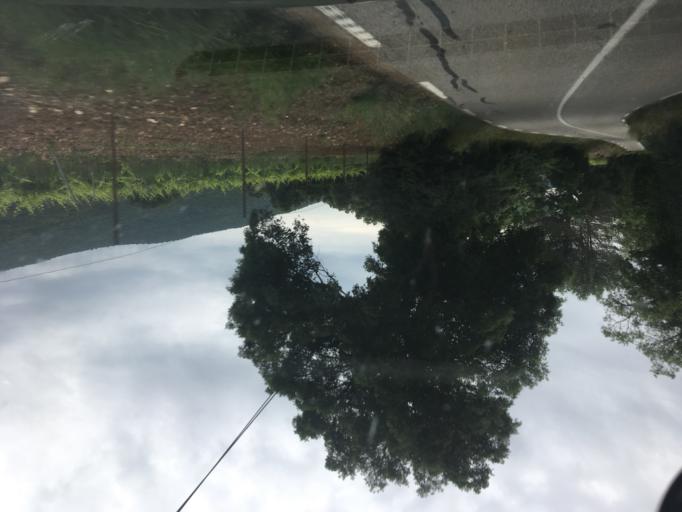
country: FR
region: Provence-Alpes-Cote d'Azur
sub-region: Departement du Var
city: Pierrefeu-du-Var
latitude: 43.2332
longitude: 6.1922
